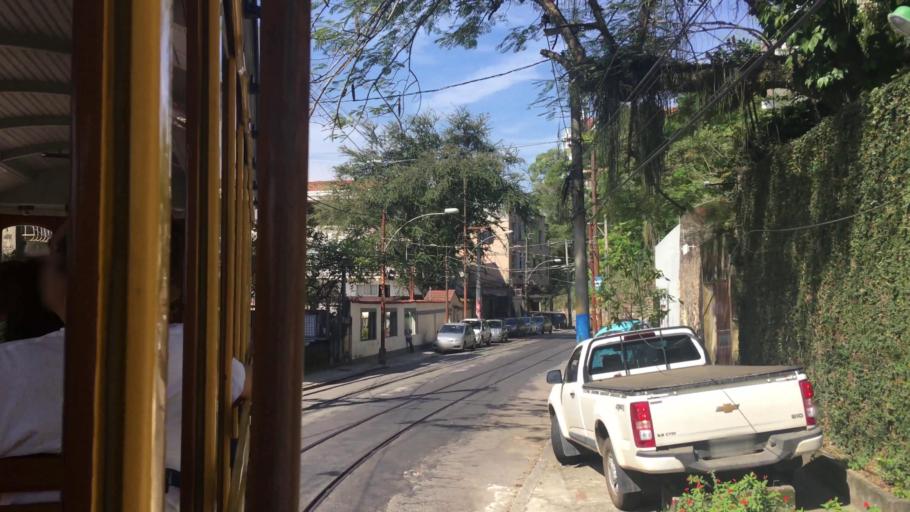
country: BR
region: Rio de Janeiro
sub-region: Rio De Janeiro
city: Rio de Janeiro
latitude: -22.9257
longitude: -43.1907
